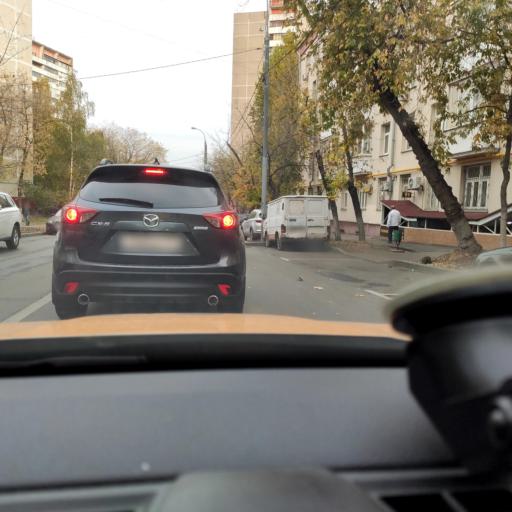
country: RU
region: Moscow
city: Tekstil'shchiki
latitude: 55.7048
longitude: 37.7400
